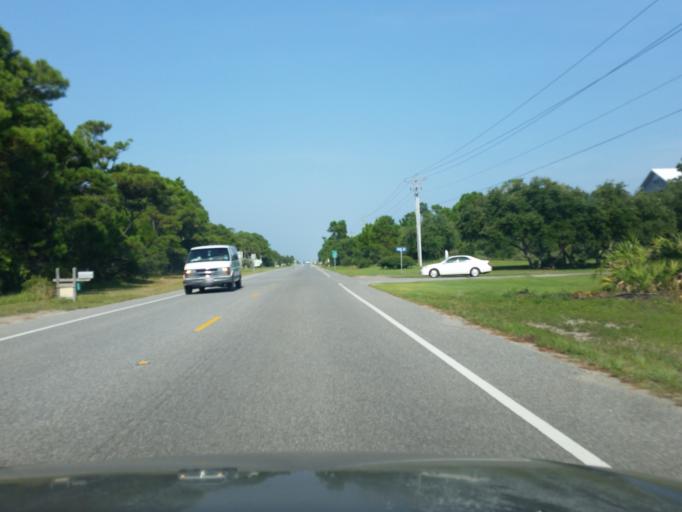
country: US
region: Alabama
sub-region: Mobile County
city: Dauphin Island
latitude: 30.2310
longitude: -87.9962
